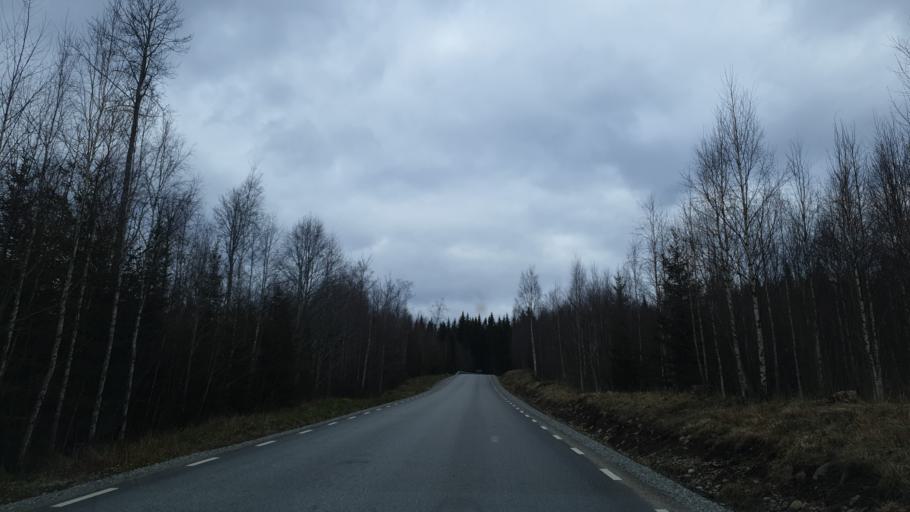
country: SE
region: OErebro
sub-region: Nora Kommun
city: Nora
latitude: 59.6172
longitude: 15.0412
